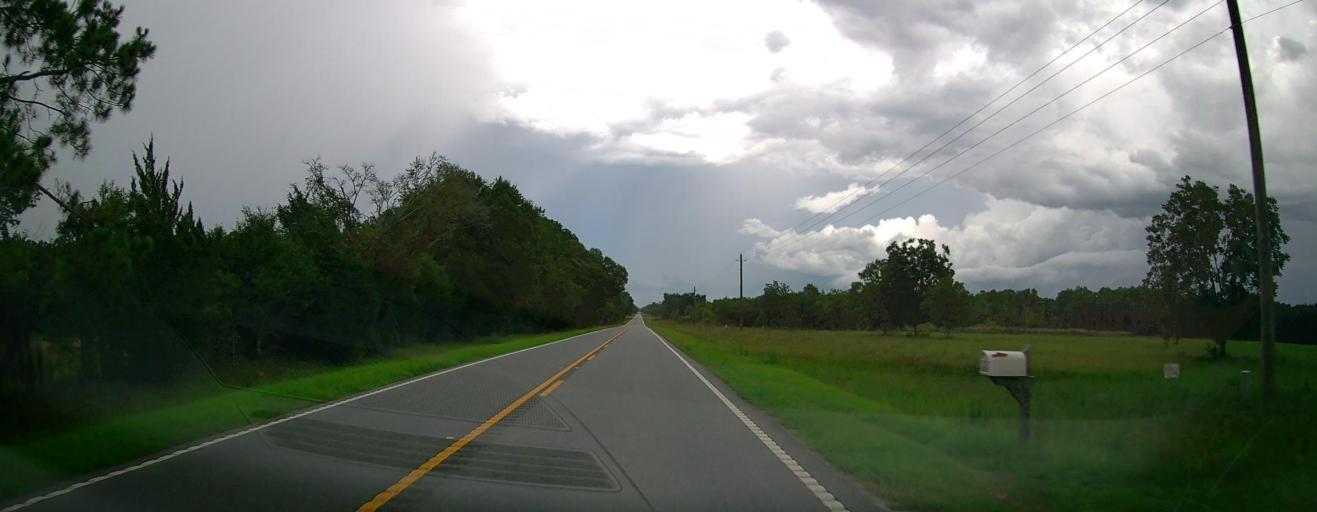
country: US
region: Georgia
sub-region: Pierce County
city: Blackshear
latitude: 31.3704
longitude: -82.1015
